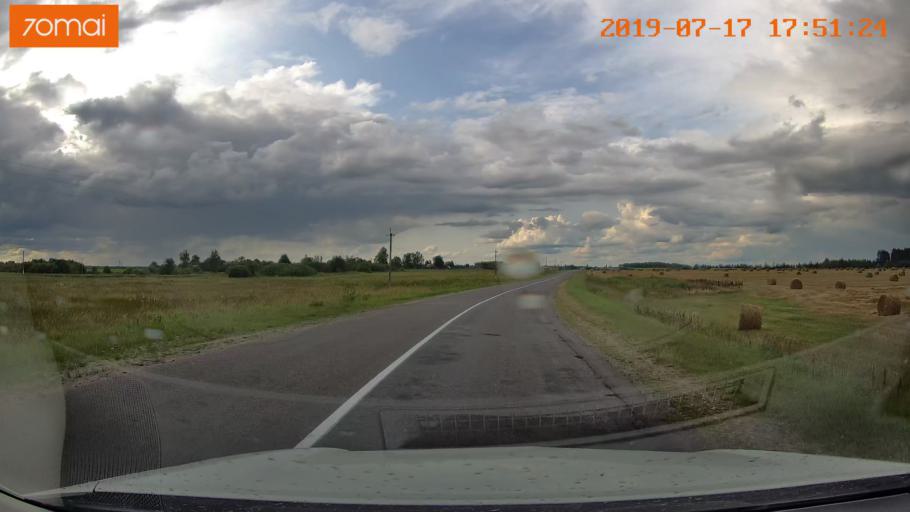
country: BY
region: Mogilev
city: Hlusha
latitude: 53.1516
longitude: 28.7884
